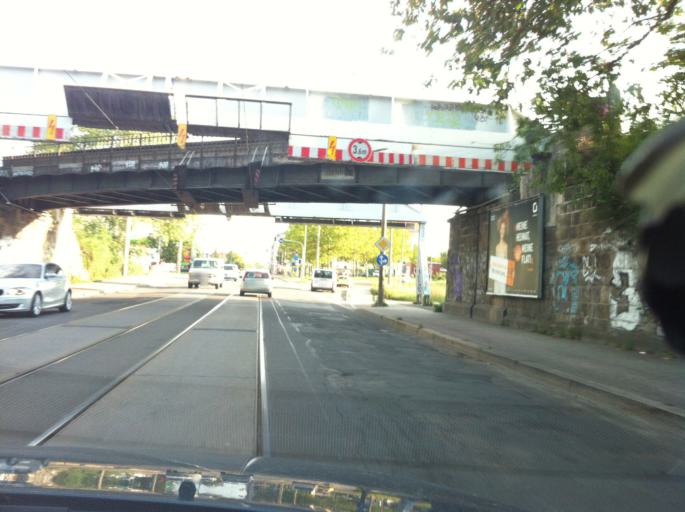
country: DE
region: Saxony
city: Leipzig
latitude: 51.3116
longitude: 12.3257
